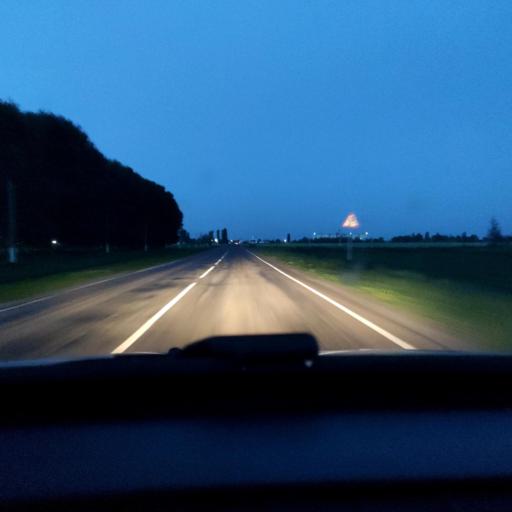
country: RU
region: Voronezj
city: Panino
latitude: 51.6505
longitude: 40.1001
